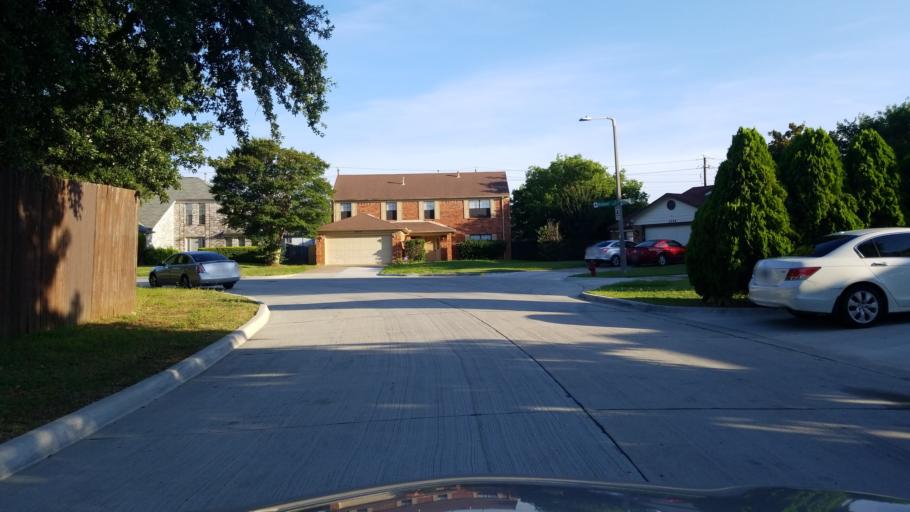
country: US
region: Texas
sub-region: Dallas County
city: Grand Prairie
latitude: 32.6922
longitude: -97.0392
